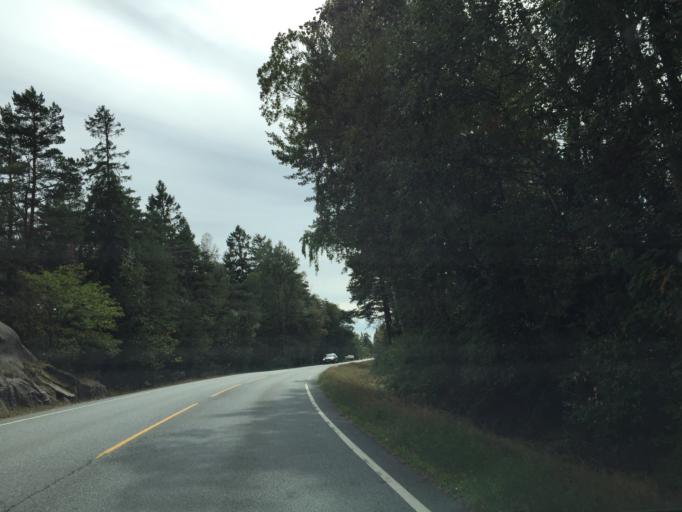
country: NO
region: Ostfold
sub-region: Fredrikstad
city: Fredrikstad
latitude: 59.0936
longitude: 10.9273
